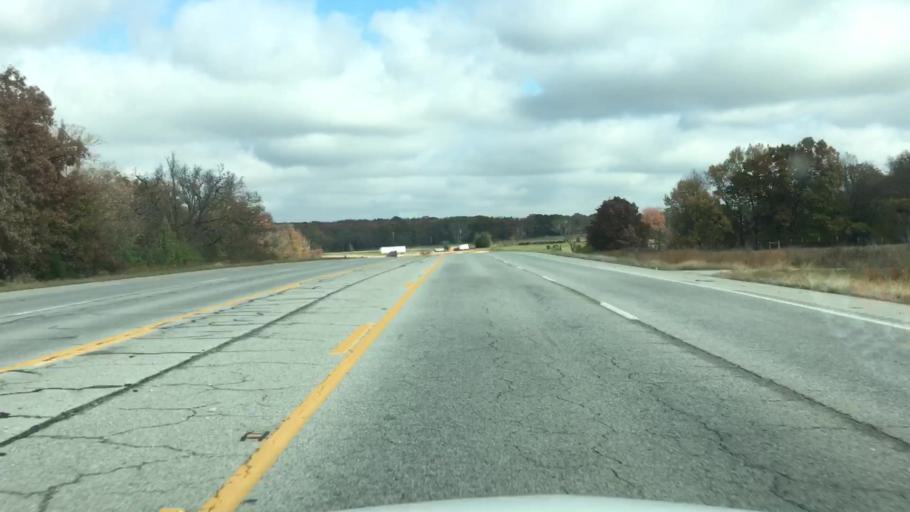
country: US
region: Arkansas
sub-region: Benton County
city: Gentry
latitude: 36.2349
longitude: -94.4905
